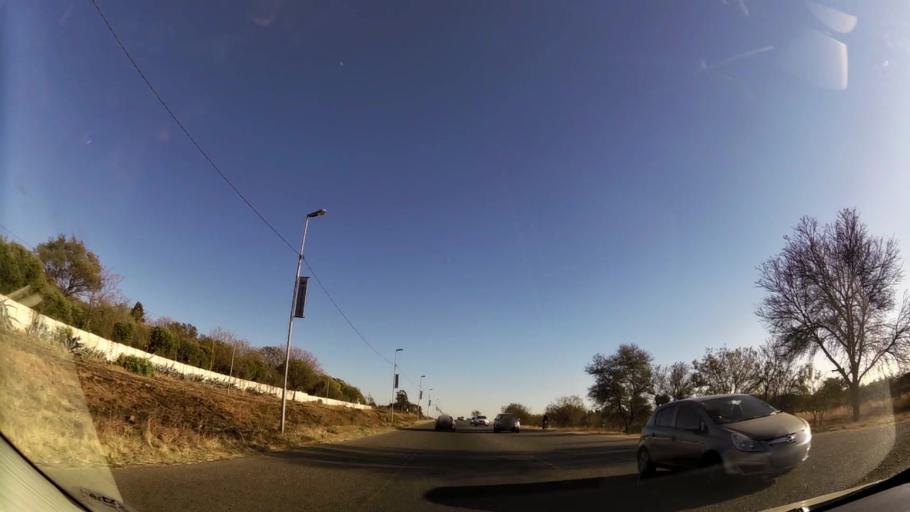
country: ZA
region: Gauteng
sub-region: West Rand District Municipality
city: Muldersdriseloop
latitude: -26.0855
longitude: 27.8646
